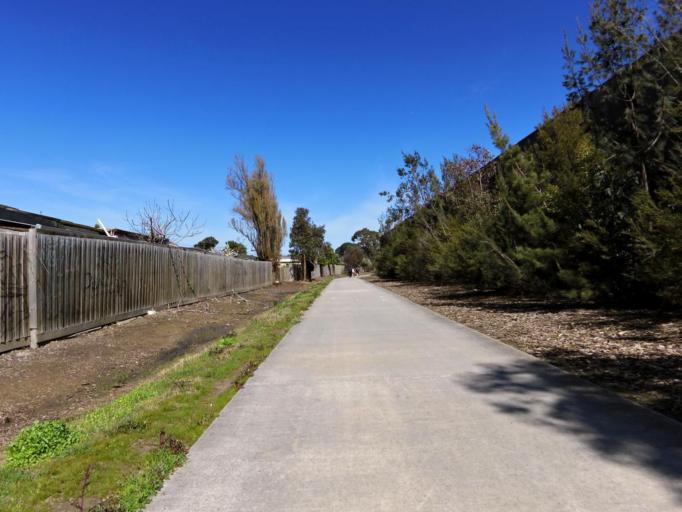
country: AU
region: Victoria
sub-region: Greater Dandenong
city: Dandenong North
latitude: -37.9581
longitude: 145.2018
